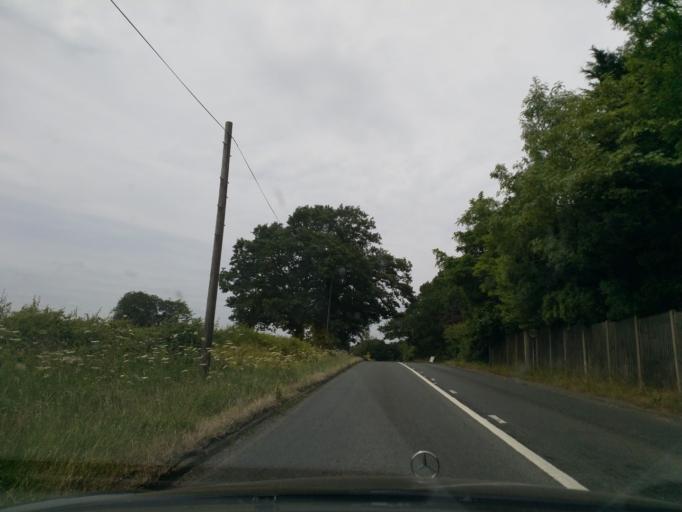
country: GB
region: England
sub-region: Solihull
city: Balsall Common
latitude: 52.3759
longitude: -1.6356
